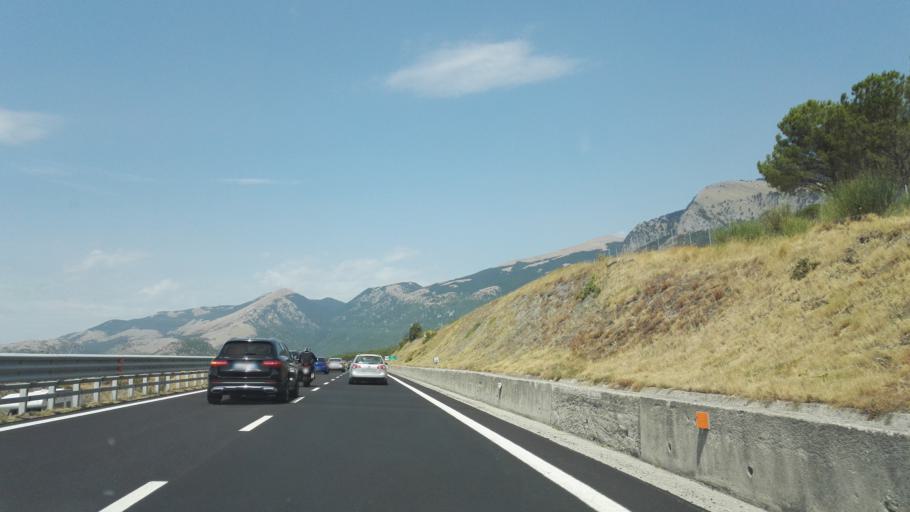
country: IT
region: Calabria
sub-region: Provincia di Cosenza
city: Castrovillari
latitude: 39.8575
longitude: 16.1972
